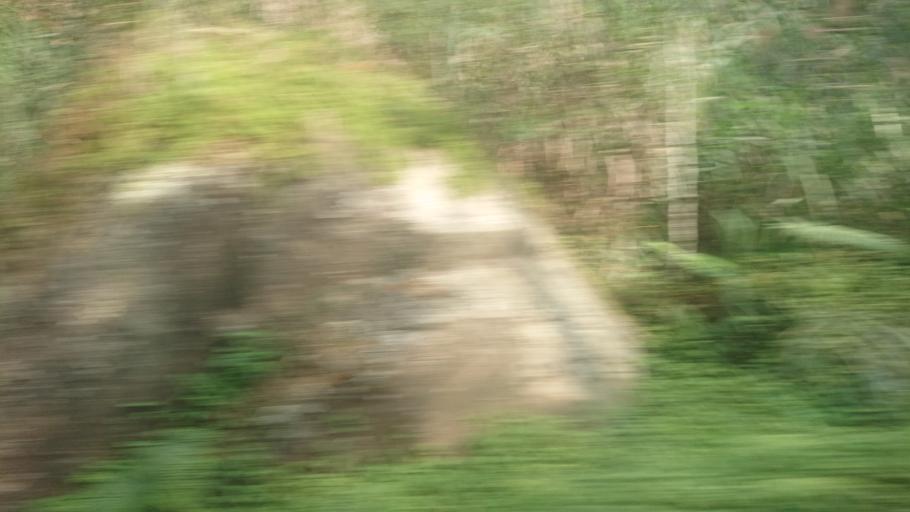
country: TW
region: Taiwan
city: Lugu
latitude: 23.5038
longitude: 120.7838
